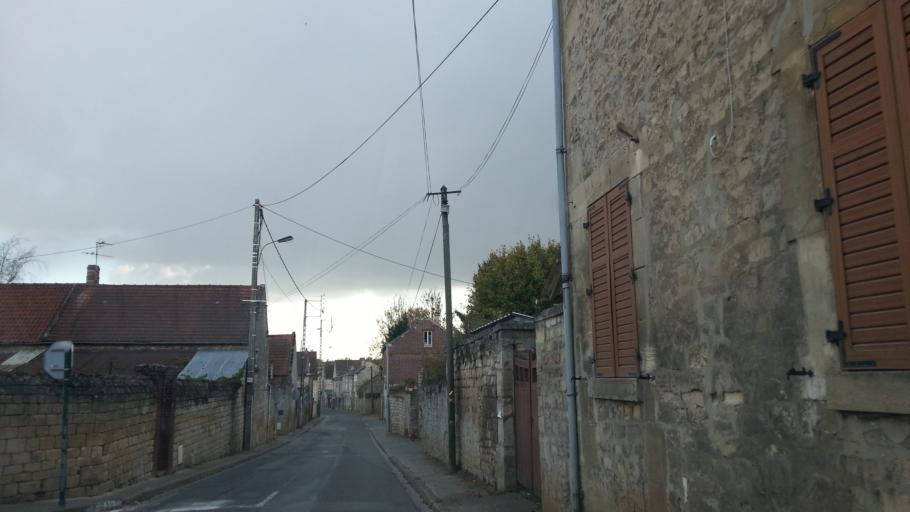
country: FR
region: Picardie
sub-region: Departement de l'Oise
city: Villers-sous-Saint-Leu
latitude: 49.2191
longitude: 2.4159
